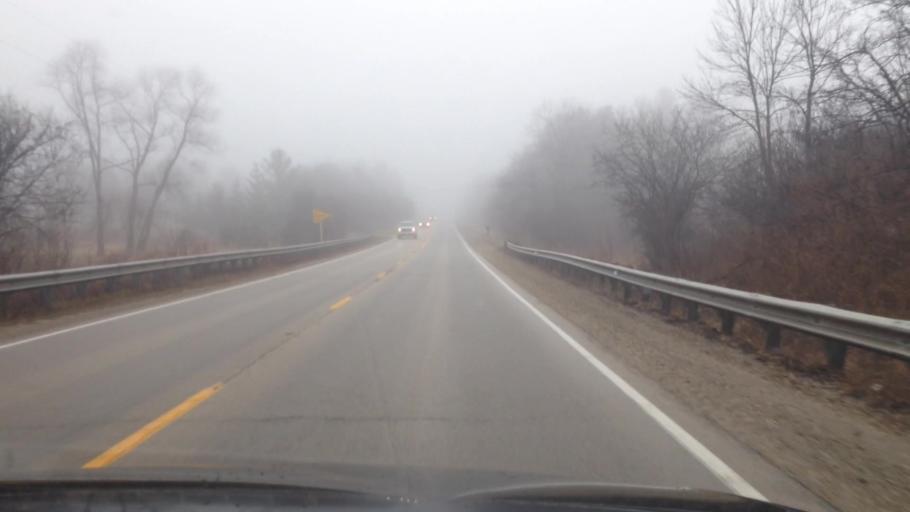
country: US
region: Illinois
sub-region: McHenry County
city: Woodstock
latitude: 42.3798
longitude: -88.4432
